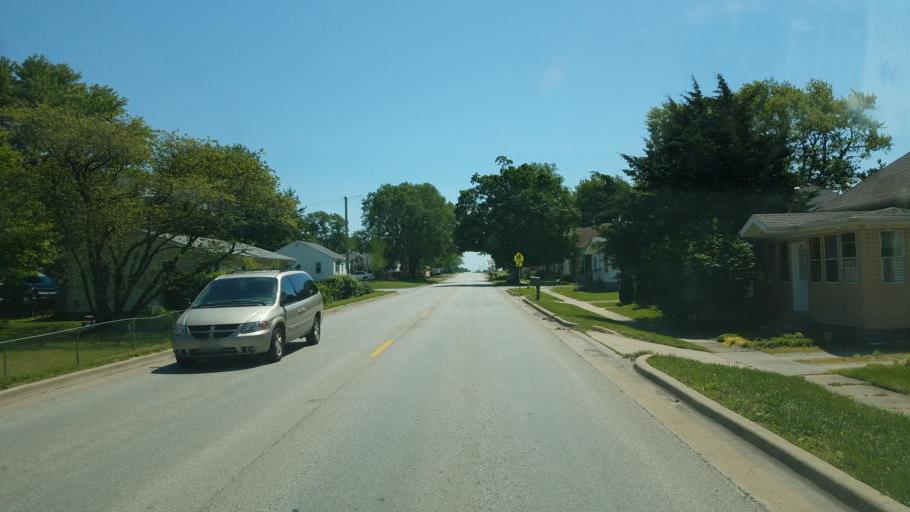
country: US
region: Illinois
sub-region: McLean County
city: Heyworth
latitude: 40.3120
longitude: -88.9746
